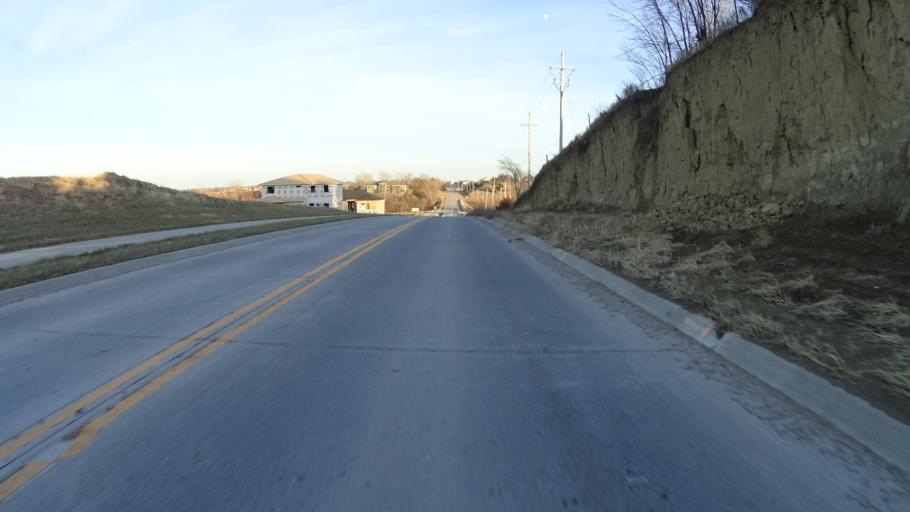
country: US
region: Nebraska
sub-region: Sarpy County
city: Papillion
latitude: 41.1327
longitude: -96.0782
